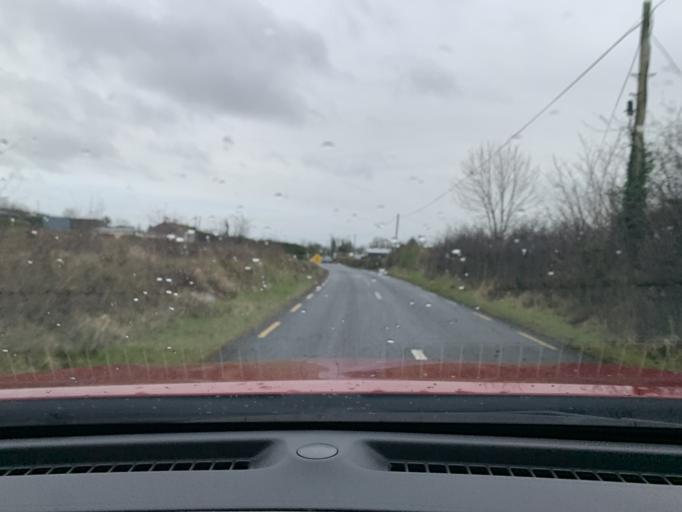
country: IE
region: Connaught
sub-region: Roscommon
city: Boyle
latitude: 53.9888
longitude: -8.3486
